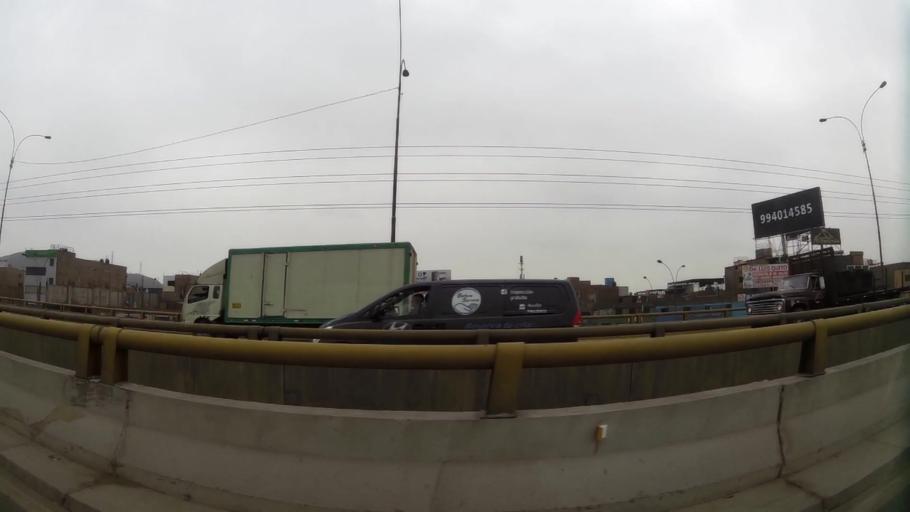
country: PE
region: Lima
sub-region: Lima
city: Independencia
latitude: -11.9898
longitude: -77.0642
